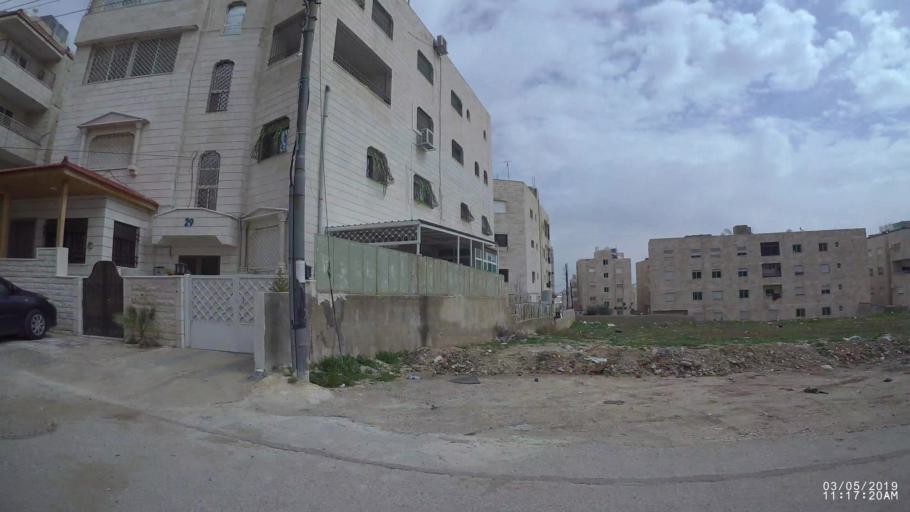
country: JO
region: Amman
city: Amman
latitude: 31.9904
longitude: 35.9270
